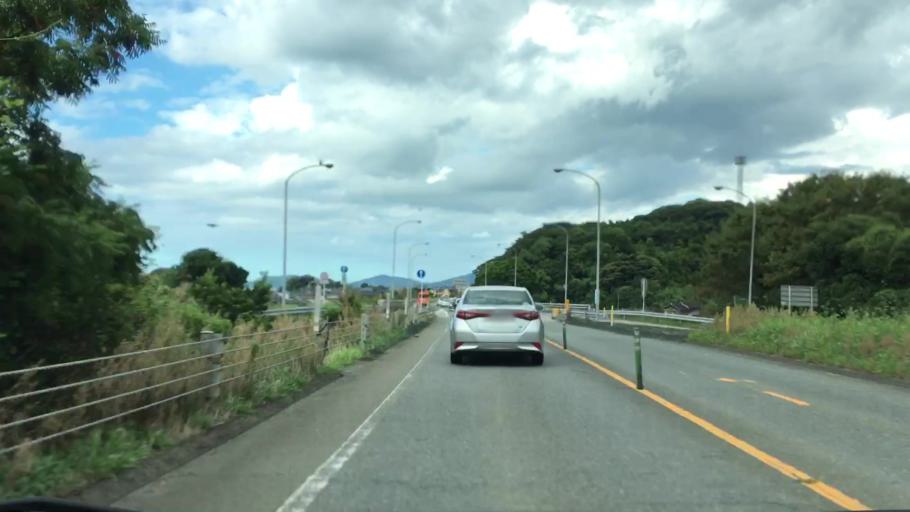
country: JP
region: Saga Prefecture
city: Karatsu
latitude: 33.4962
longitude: 130.0792
